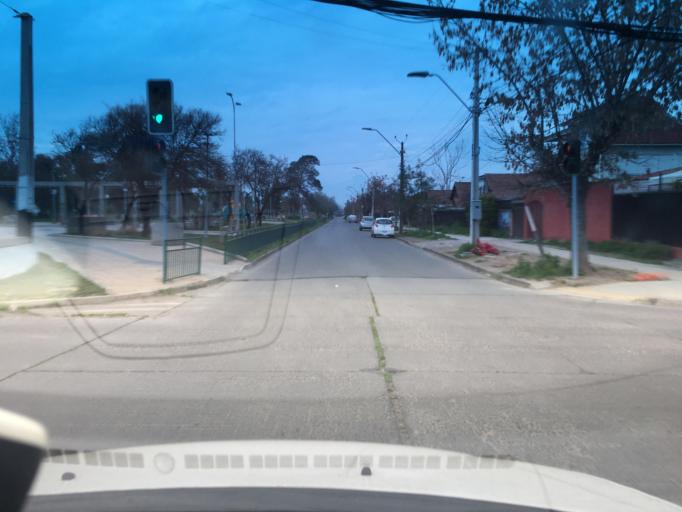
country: CL
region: Santiago Metropolitan
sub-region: Provincia de Santiago
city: Villa Presidente Frei, Nunoa, Santiago, Chile
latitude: -33.5019
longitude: -70.6056
